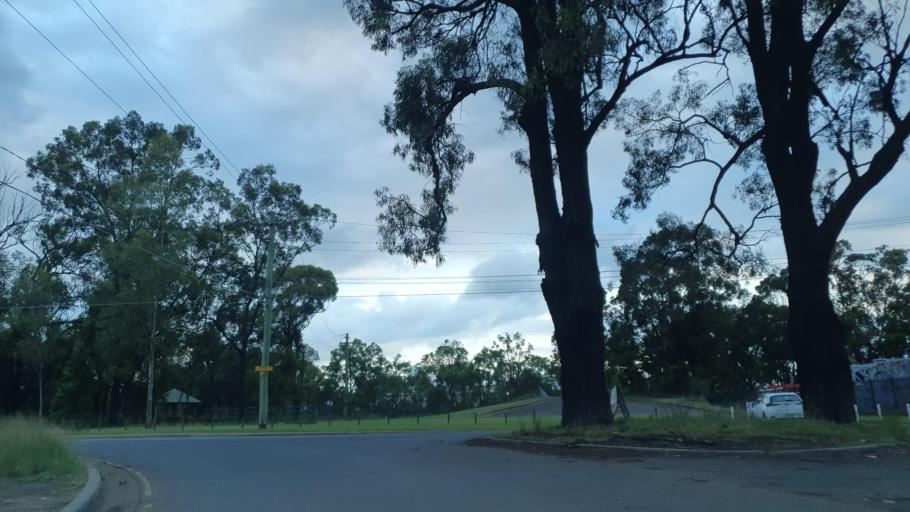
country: AU
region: New South Wales
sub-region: Penrith Municipality
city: Werrington County
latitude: -33.7454
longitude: 150.7713
